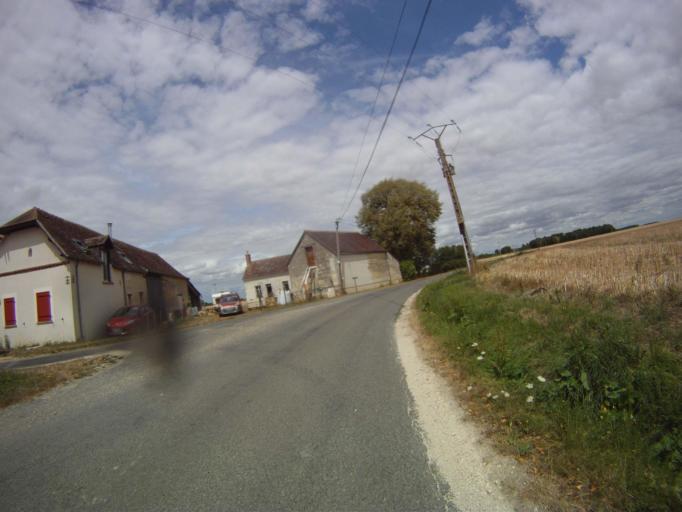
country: FR
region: Centre
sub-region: Departement du Loir-et-Cher
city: Montoire-sur-le-Loir
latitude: 47.6896
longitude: 0.8072
